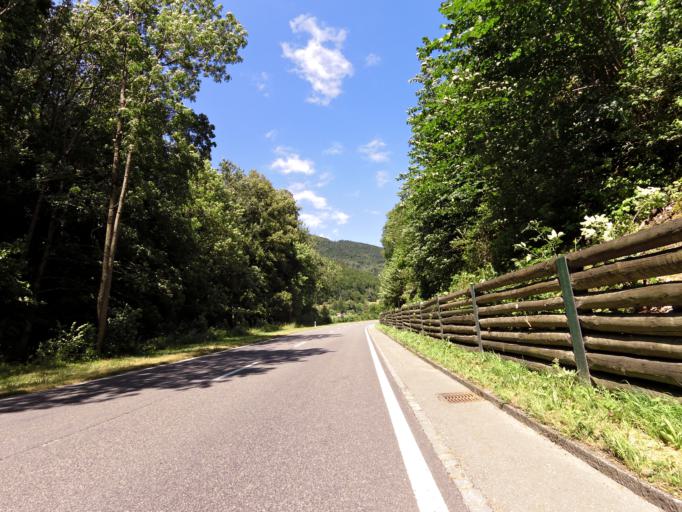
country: CH
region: Solothurn
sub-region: Bezirk Gaeu
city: Oberbuchsiten
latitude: 47.3287
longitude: 7.7367
